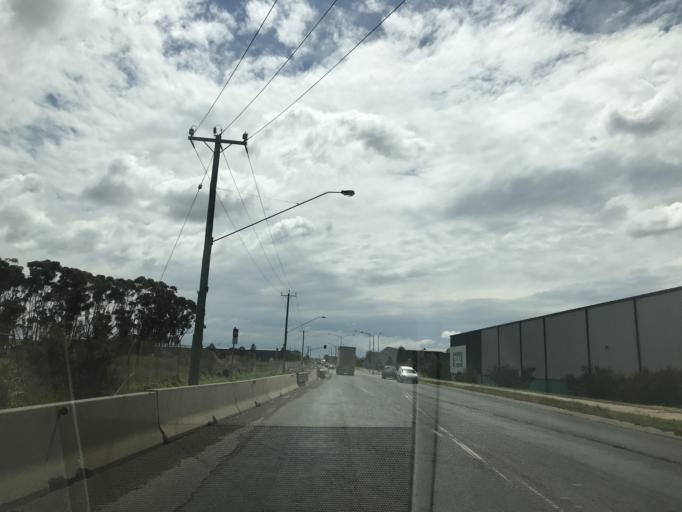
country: AU
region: Victoria
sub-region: Wyndham
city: Truganina
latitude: -37.8178
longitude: 144.7499
